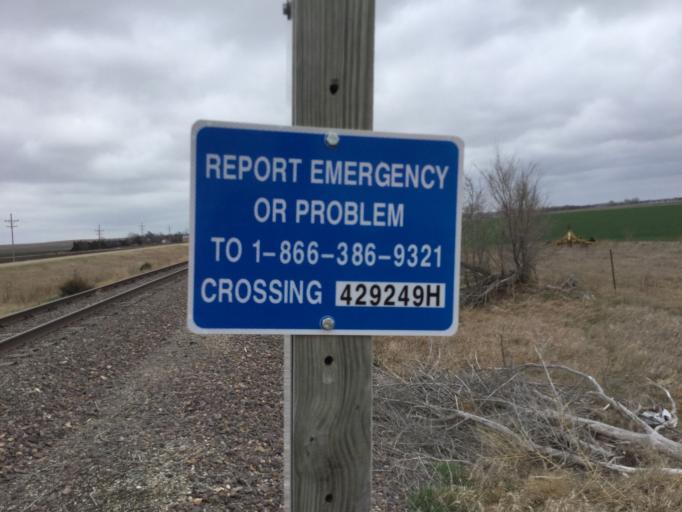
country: US
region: Kansas
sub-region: Barton County
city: Hoisington
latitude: 38.5218
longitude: -98.6646
